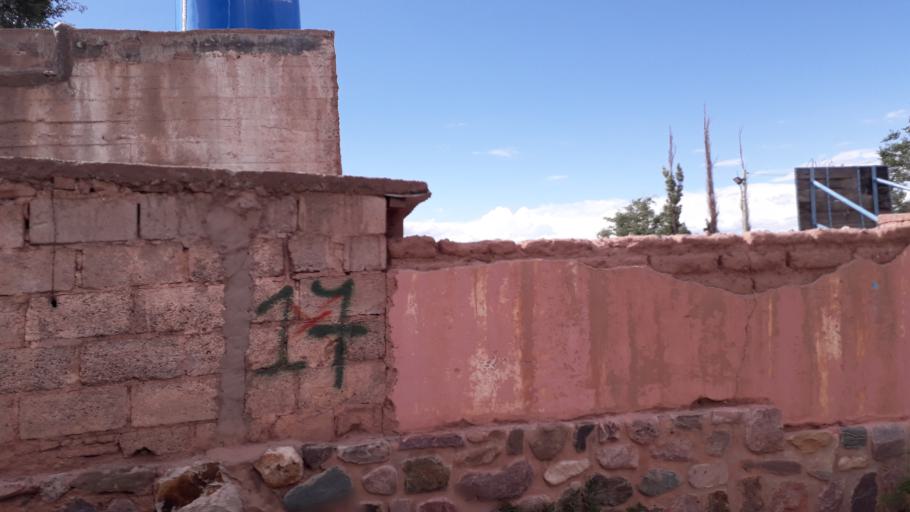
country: AR
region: Jujuy
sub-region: Departamento de Humahuaca
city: Humahuaca
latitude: -23.3050
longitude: -65.3573
